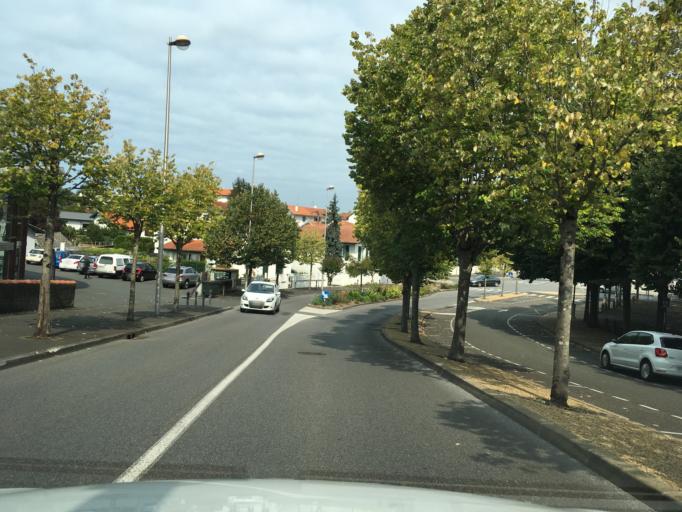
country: FR
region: Aquitaine
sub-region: Departement des Pyrenees-Atlantiques
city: Anglet
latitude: 43.4834
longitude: -1.5135
